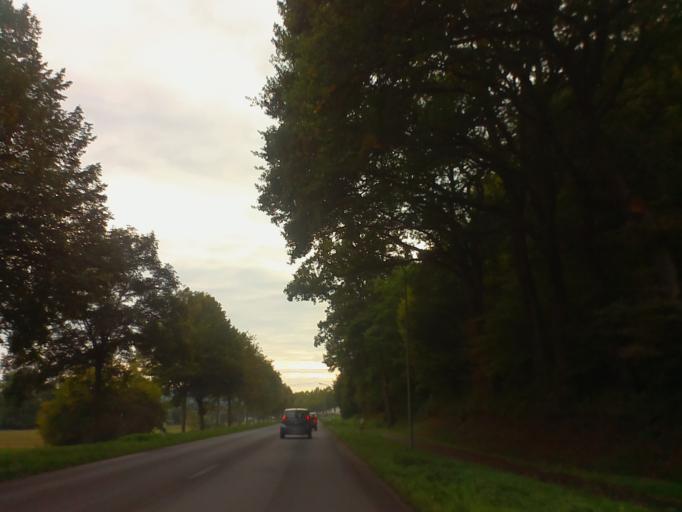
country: DE
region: Hesse
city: Hochst im Odenwald
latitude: 49.8116
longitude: 9.0074
